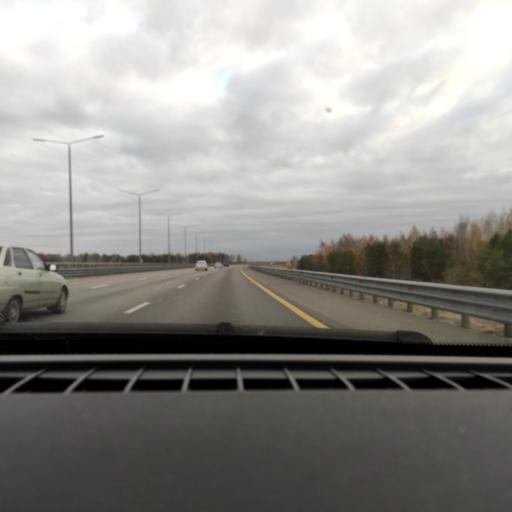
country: RU
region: Voronezj
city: Somovo
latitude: 51.7843
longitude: 39.2895
